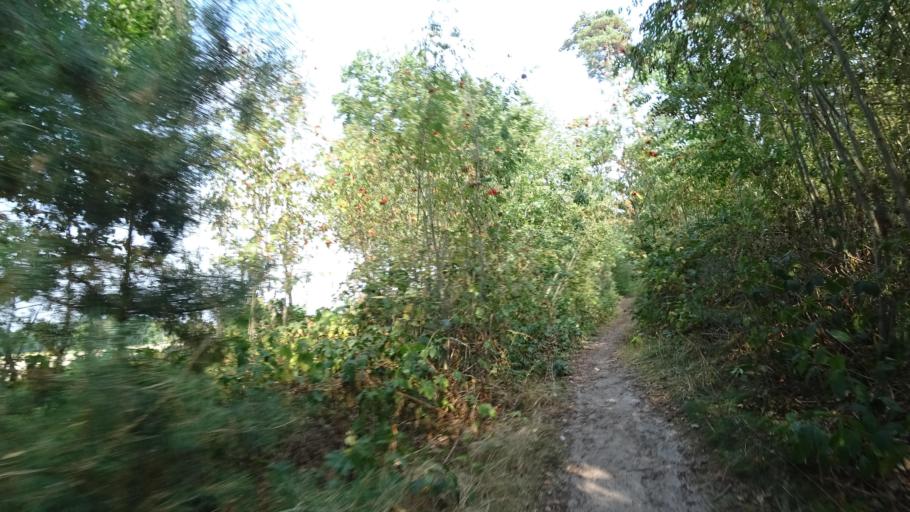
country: DE
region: North Rhine-Westphalia
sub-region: Regierungsbezirk Detmold
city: Guetersloh
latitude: 51.9330
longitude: 8.4321
